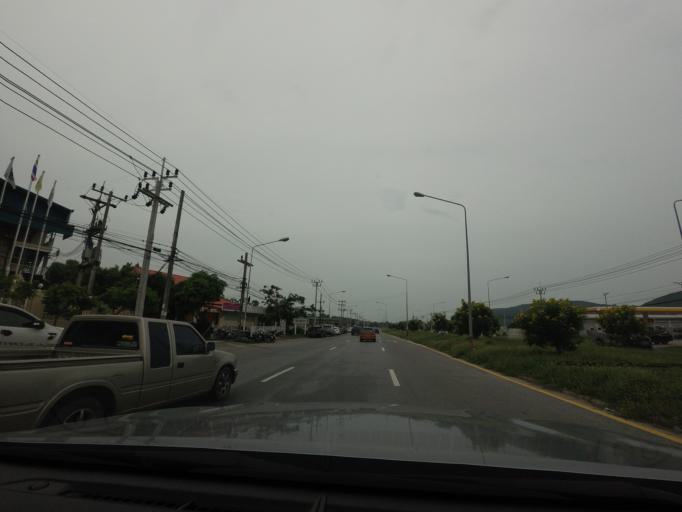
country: TH
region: Songkhla
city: Ban Mai
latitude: 7.2044
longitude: 100.5544
